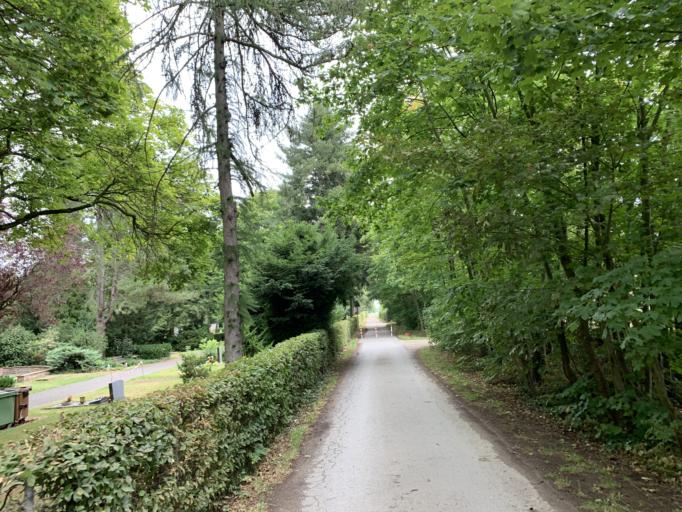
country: DE
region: North Rhine-Westphalia
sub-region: Regierungsbezirk Koln
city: Dueren
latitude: 50.8035
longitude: 6.5087
